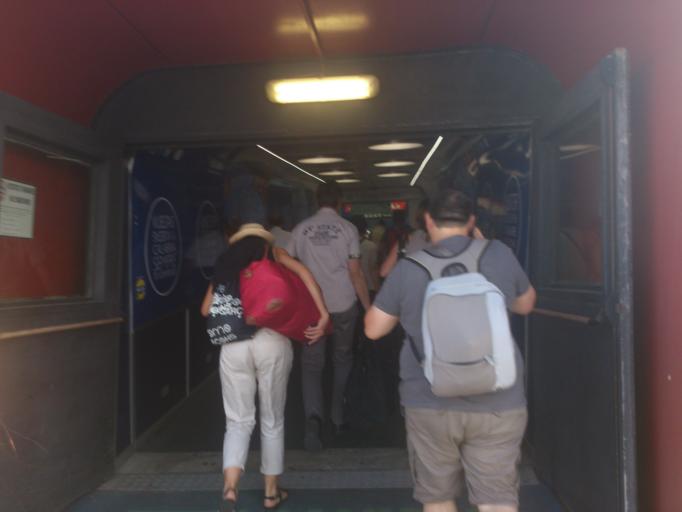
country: IT
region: Calabria
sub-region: Provincia di Catanzaro
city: Santa Eufemia Lamezia
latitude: 38.9093
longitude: 16.2461
